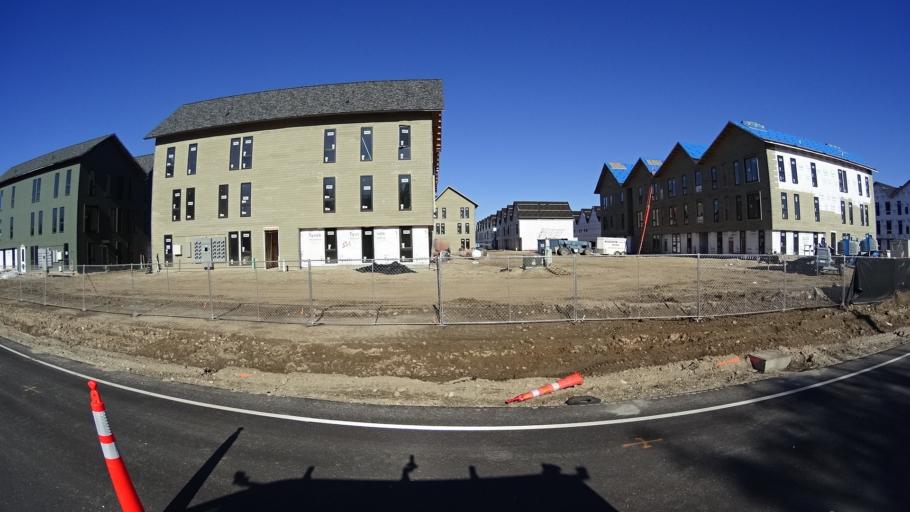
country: US
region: Idaho
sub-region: Ada County
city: Eagle
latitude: 43.6919
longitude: -116.4137
